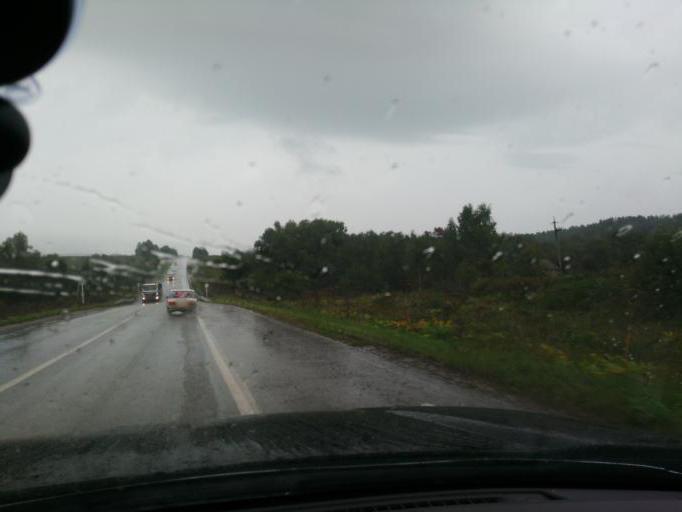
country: RU
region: Perm
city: Osa
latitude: 57.1467
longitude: 55.5292
